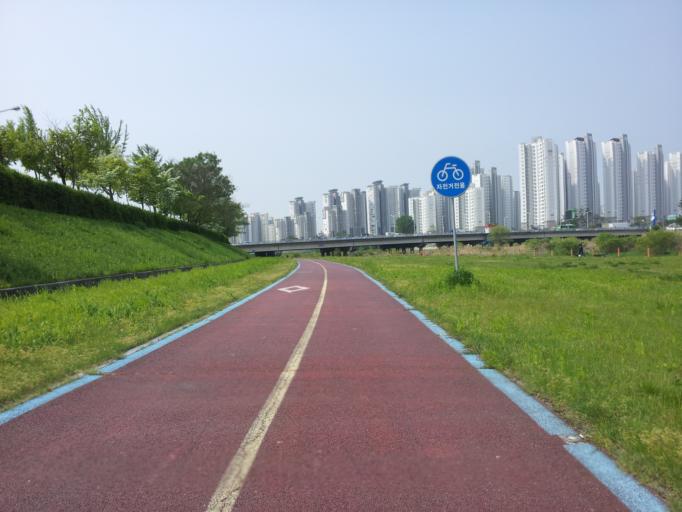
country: KR
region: Daejeon
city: Daejeon
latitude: 36.3531
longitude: 127.3521
